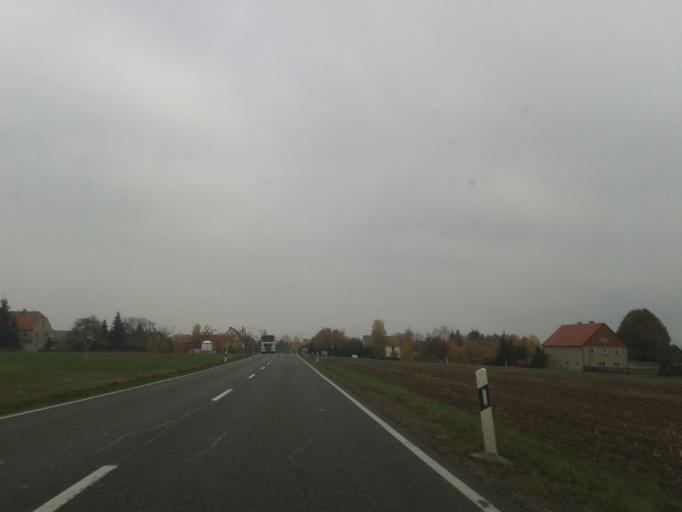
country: DE
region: Saxony
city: Niederschona
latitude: 50.9764
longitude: 13.4413
